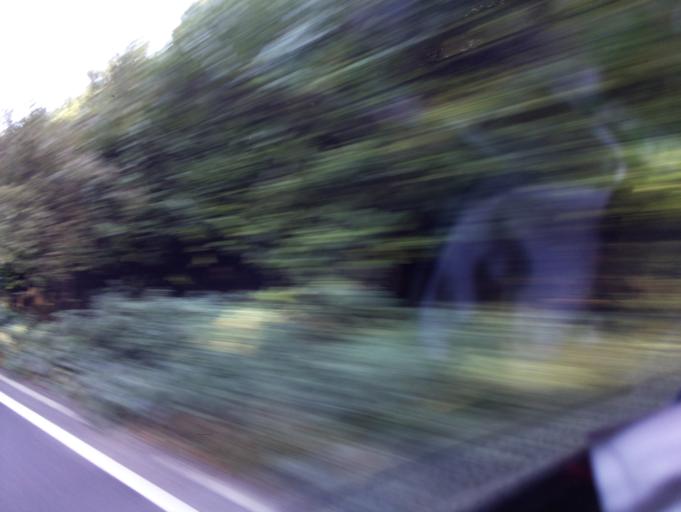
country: GB
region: England
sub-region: Hampshire
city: Swanmore
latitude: 51.0005
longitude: -1.1178
